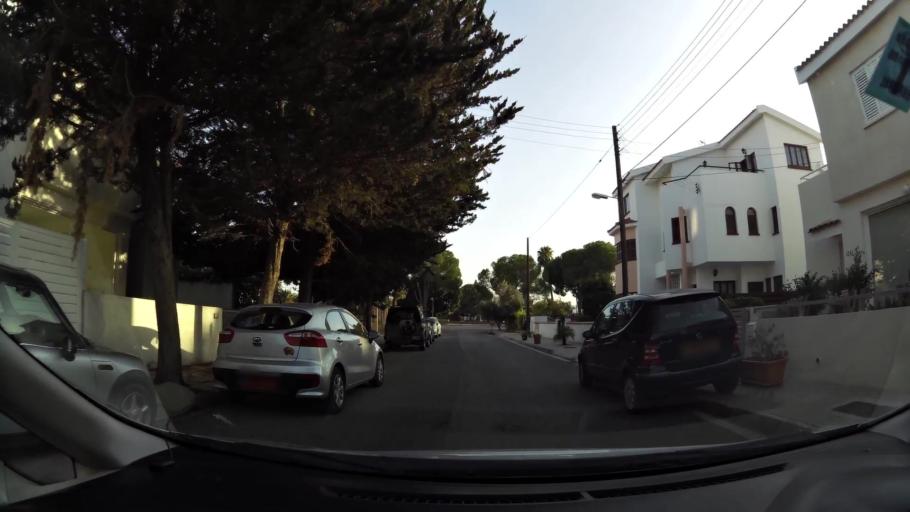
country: CY
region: Lefkosia
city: Nicosia
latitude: 35.1651
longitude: 33.3254
